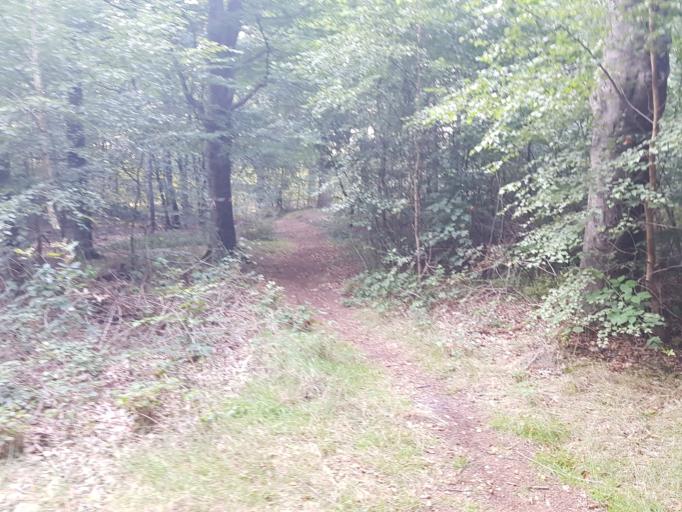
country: NL
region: Utrecht
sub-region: Gemeente Veenendaal
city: Veenendaal
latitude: 51.9912
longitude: 5.5400
